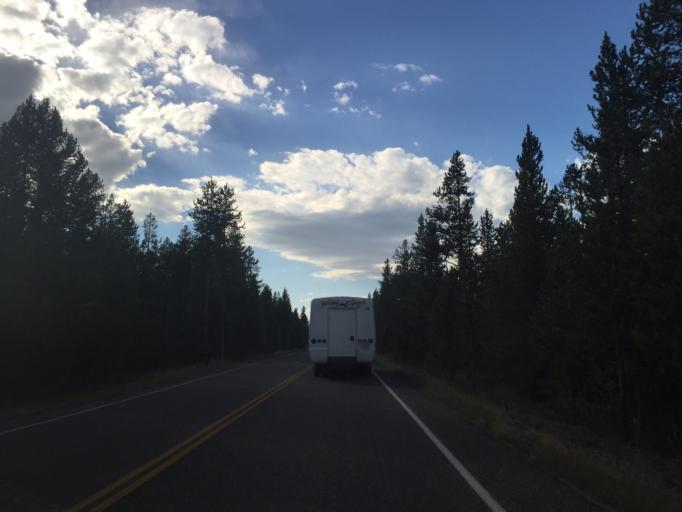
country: US
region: Montana
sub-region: Gallatin County
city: West Yellowstone
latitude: 44.6561
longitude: -111.0848
